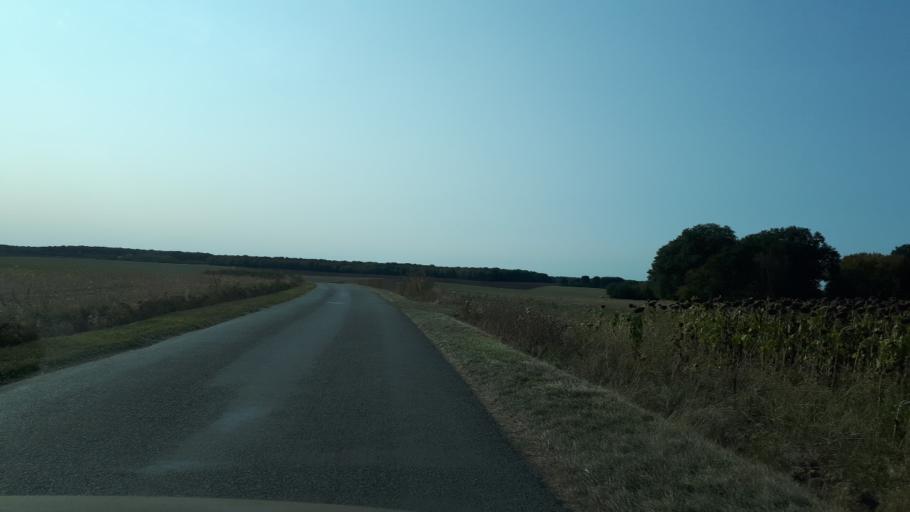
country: FR
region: Centre
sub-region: Departement du Cher
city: Rians
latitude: 47.1846
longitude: 2.6700
